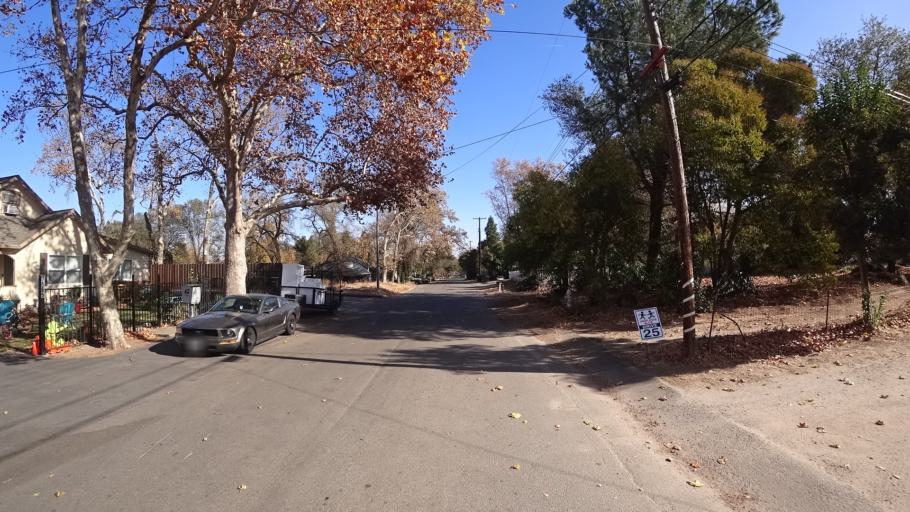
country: US
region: California
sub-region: Sacramento County
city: Citrus Heights
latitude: 38.7047
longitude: -121.2874
